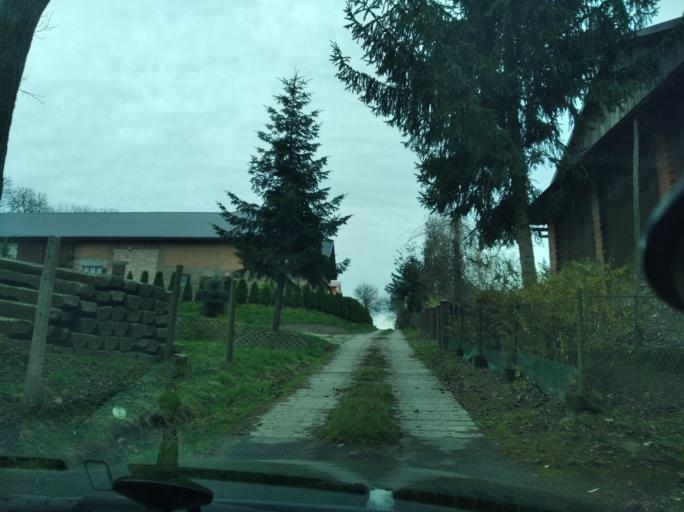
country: PL
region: Subcarpathian Voivodeship
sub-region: Powiat lancucki
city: Markowa
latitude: 50.0203
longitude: 22.3180
